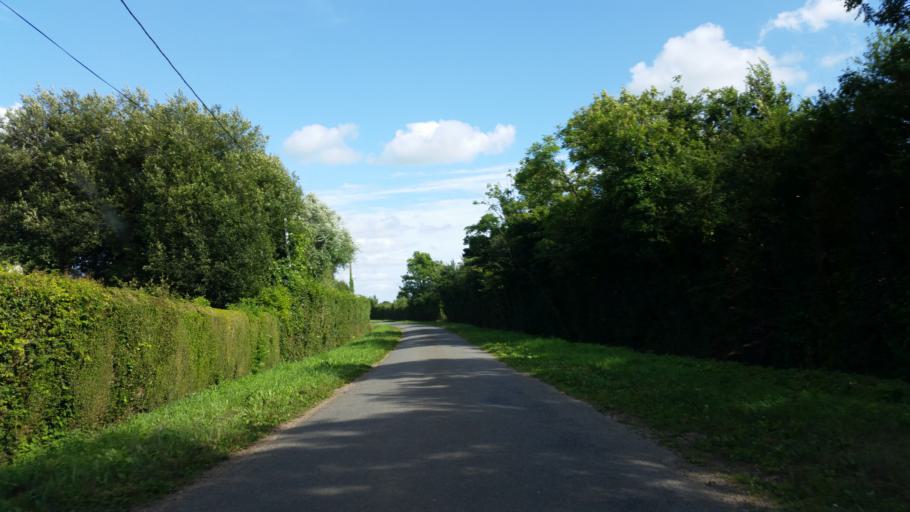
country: FR
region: Lower Normandy
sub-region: Departement de la Manche
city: Sainte-Mere-Eglise
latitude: 49.4593
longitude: -1.2980
